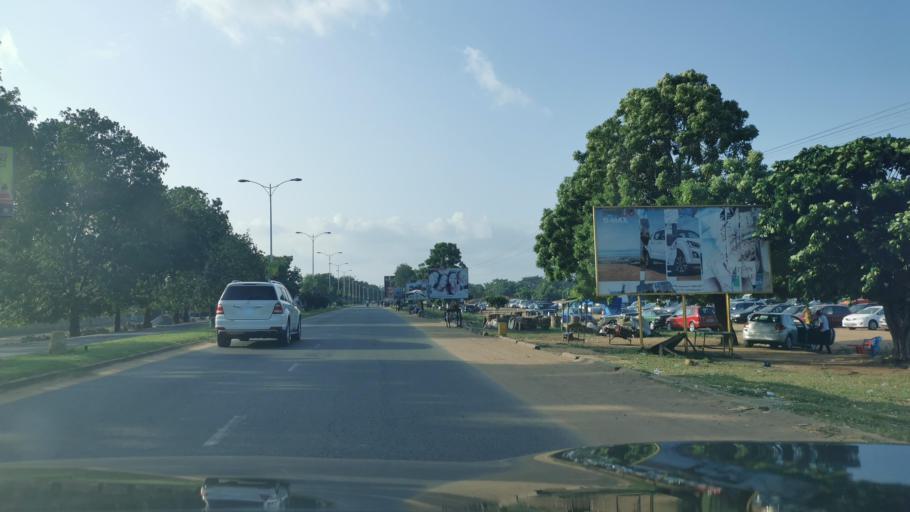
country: TG
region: Maritime
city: Lome
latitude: 6.1986
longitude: 1.2088
